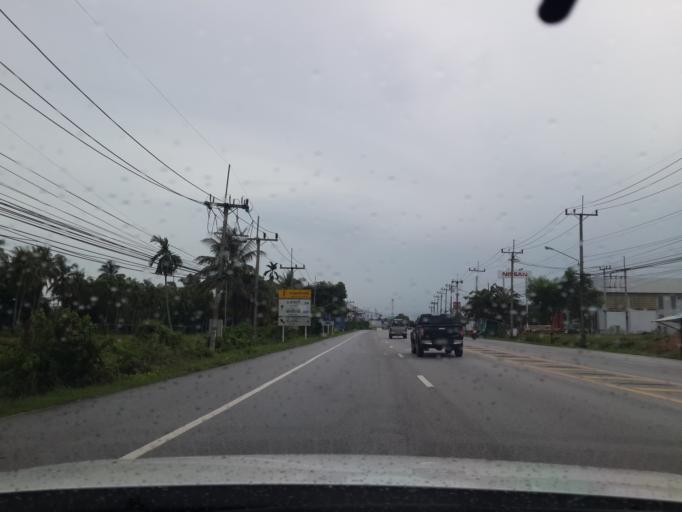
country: TH
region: Pattani
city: Nong Chik
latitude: 6.8539
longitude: 101.2125
